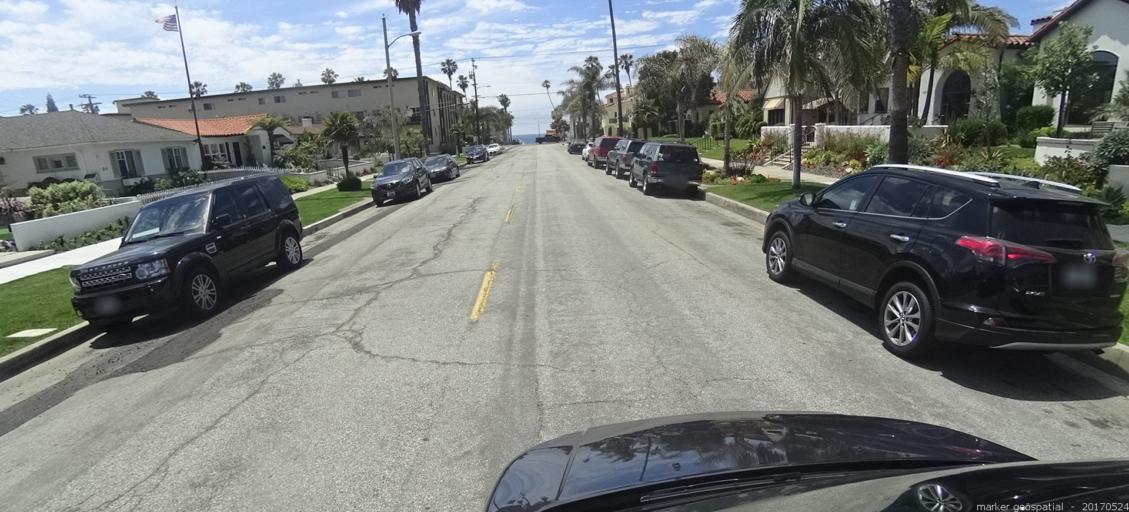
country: US
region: California
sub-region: Los Angeles County
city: Palos Verdes Estates
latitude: 33.8235
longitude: -118.3870
